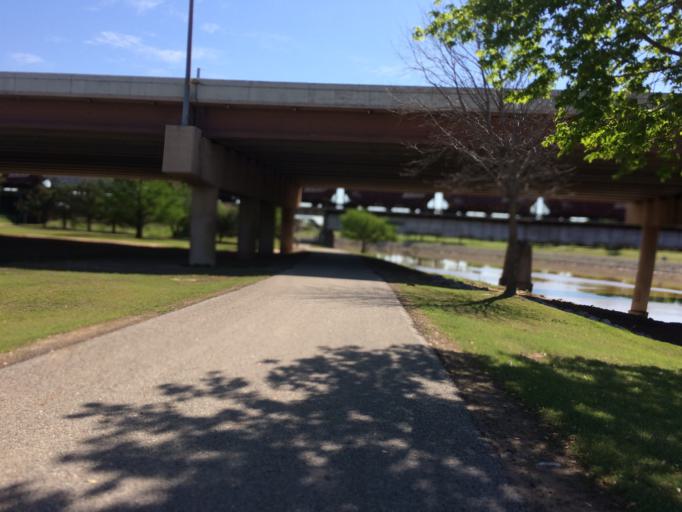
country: US
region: Oklahoma
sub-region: Oklahoma County
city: Oklahoma City
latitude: 35.4493
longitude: -97.5141
